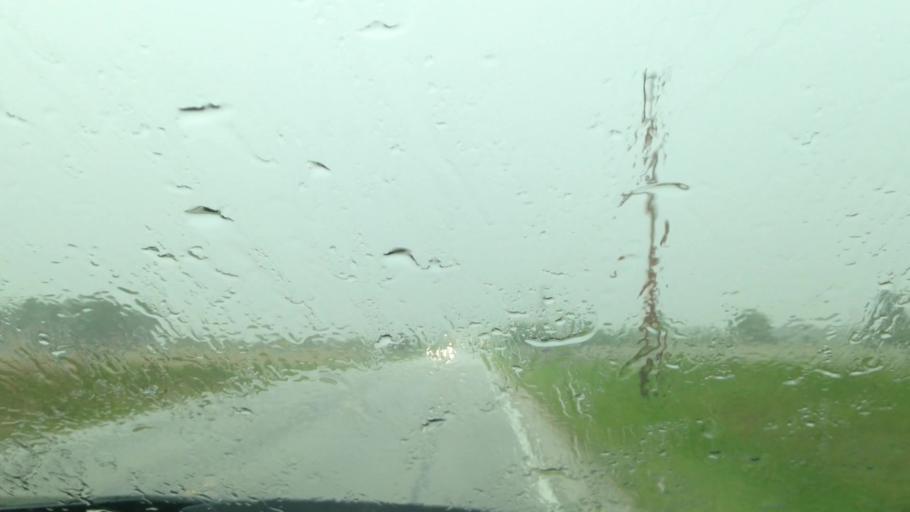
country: US
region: Ohio
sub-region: Darke County
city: Greenville
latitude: 40.1506
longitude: -84.6168
